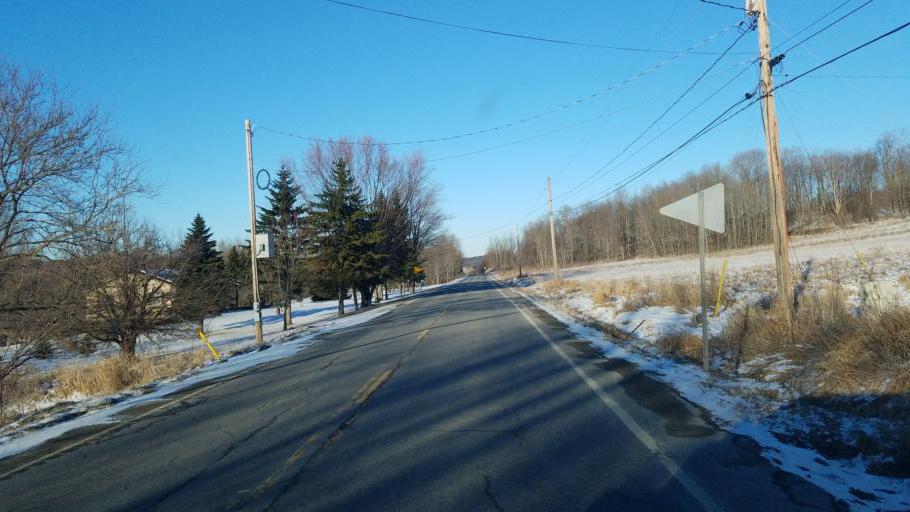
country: US
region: Pennsylvania
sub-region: Tioga County
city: Westfield
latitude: 41.9322
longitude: -77.7222
